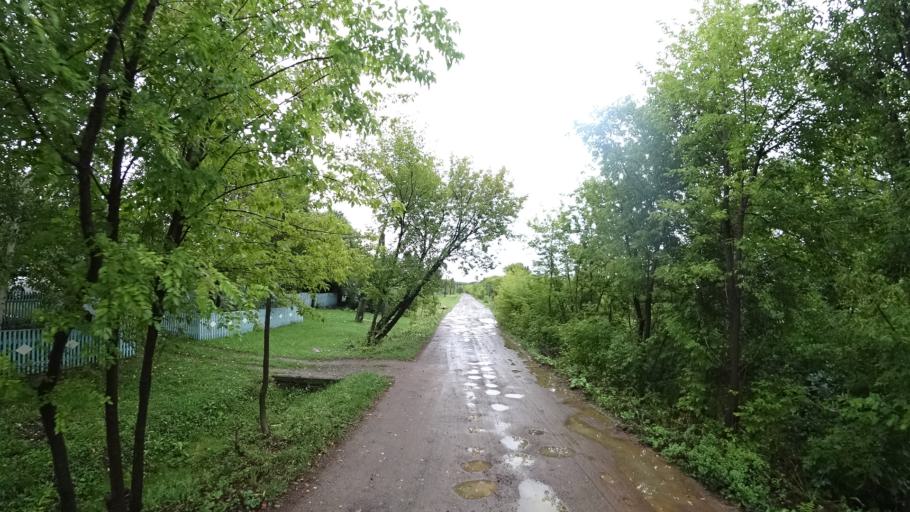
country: RU
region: Primorskiy
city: Monastyrishche
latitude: 44.2603
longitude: 132.4242
